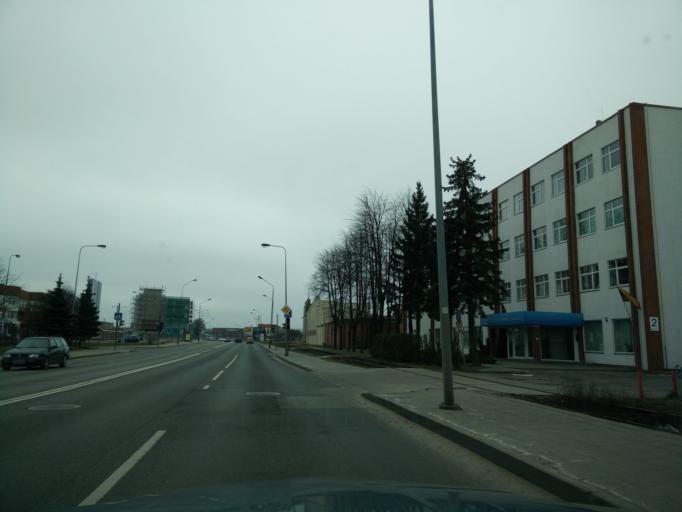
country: LT
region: Klaipedos apskritis
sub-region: Klaipeda
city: Klaipeda
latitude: 55.6997
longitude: 21.1355
